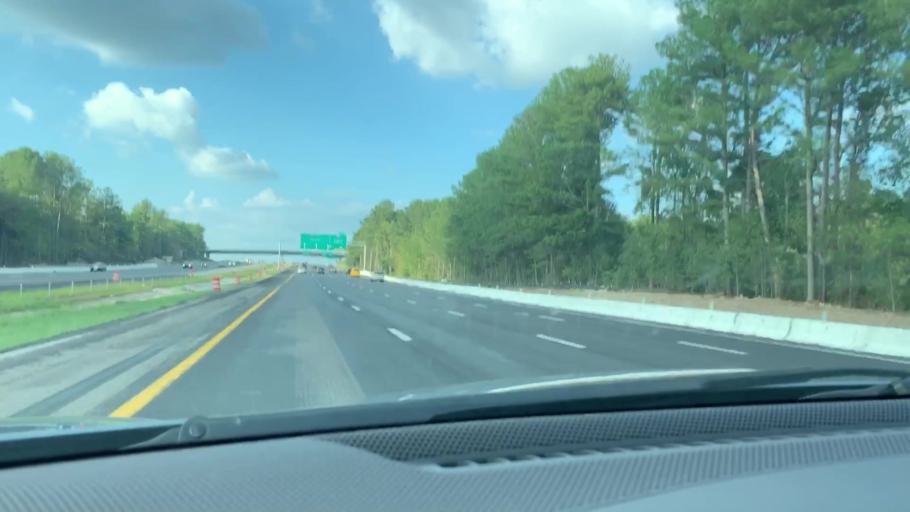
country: US
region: South Carolina
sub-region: Richland County
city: Woodfield
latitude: 34.0588
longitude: -80.9223
